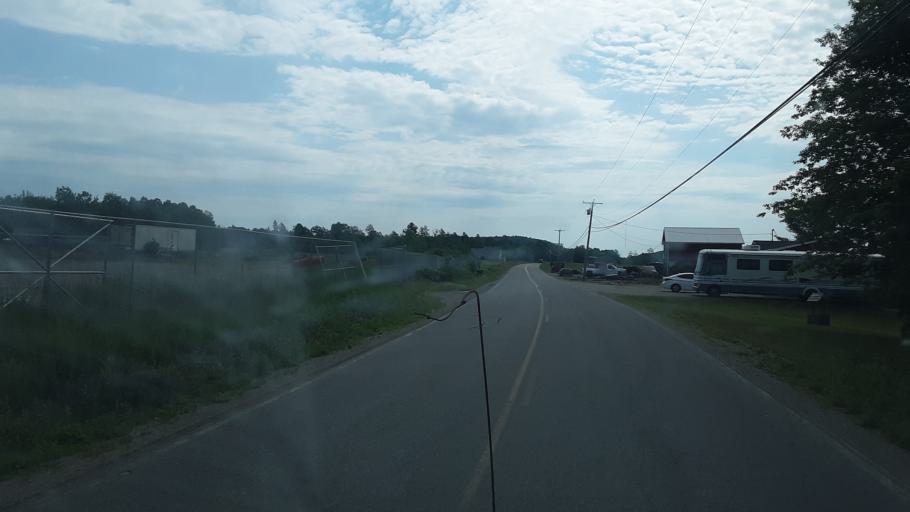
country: US
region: Maine
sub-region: Waldo County
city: Frankfort
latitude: 44.6144
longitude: -68.9374
